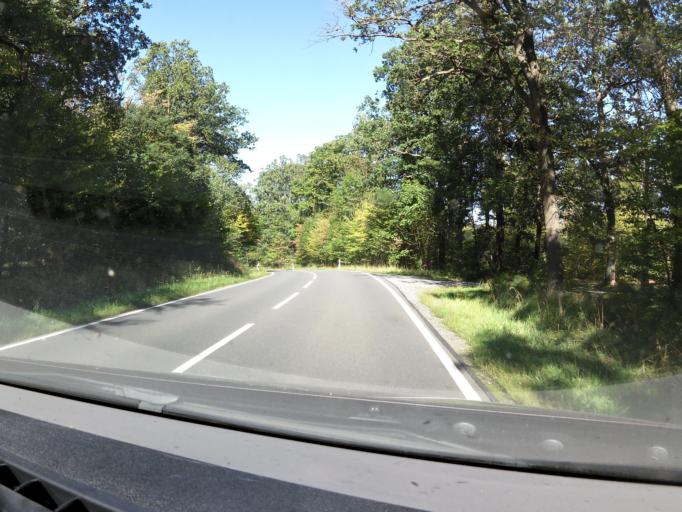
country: DE
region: Saxony-Anhalt
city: Gernrode
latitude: 51.7019
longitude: 11.1309
